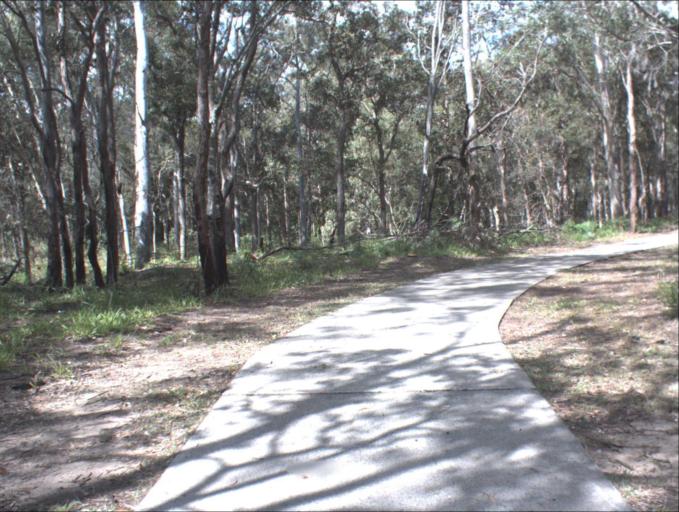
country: AU
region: Queensland
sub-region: Logan
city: Woodridge
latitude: -27.6726
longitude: 153.0575
